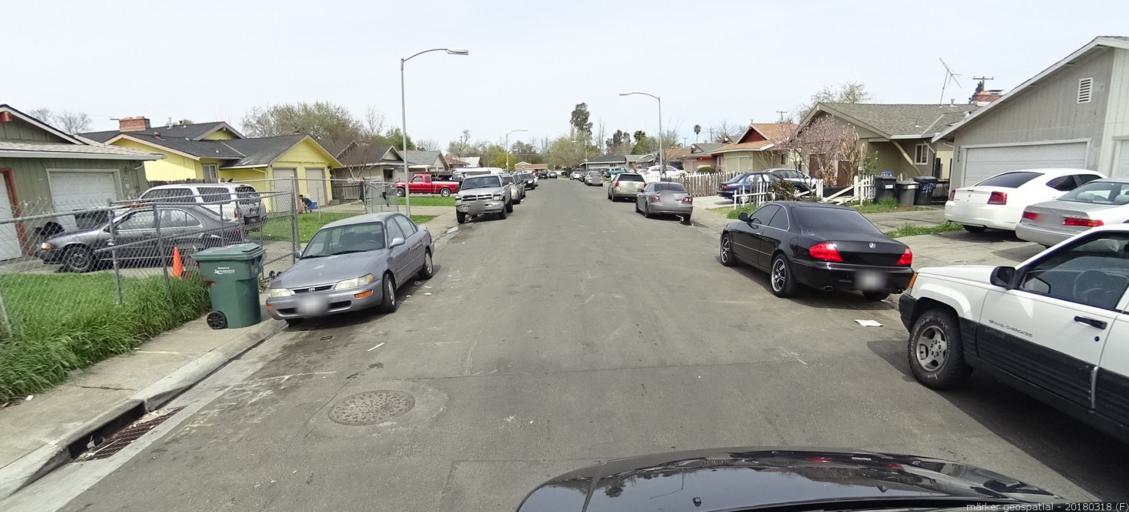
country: US
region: California
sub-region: Sacramento County
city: Parkway
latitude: 38.5181
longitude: -121.4466
